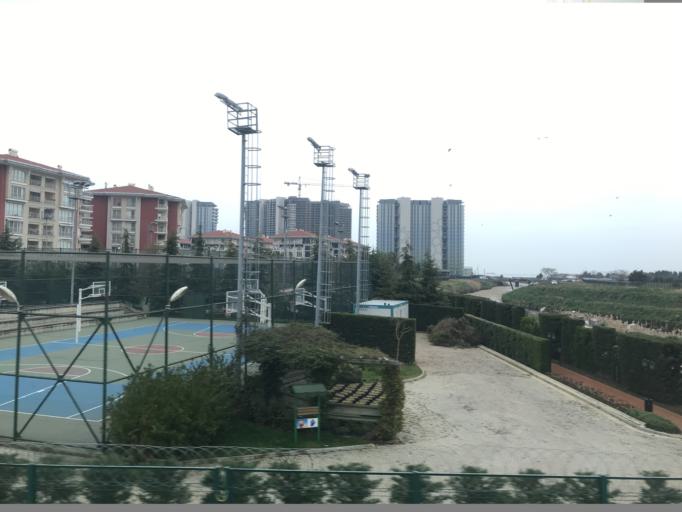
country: TR
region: Istanbul
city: Bahcelievler
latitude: 40.9766
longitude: 28.8443
